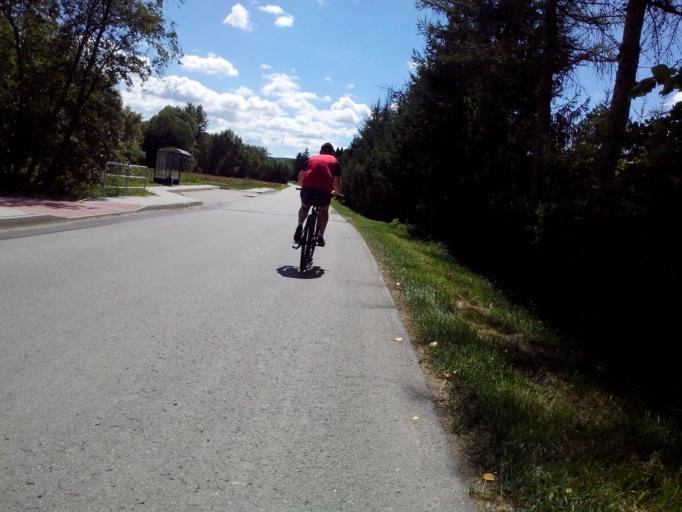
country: PL
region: Subcarpathian Voivodeship
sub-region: Powiat brzozowski
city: Blizne
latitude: 49.7822
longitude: 21.9912
